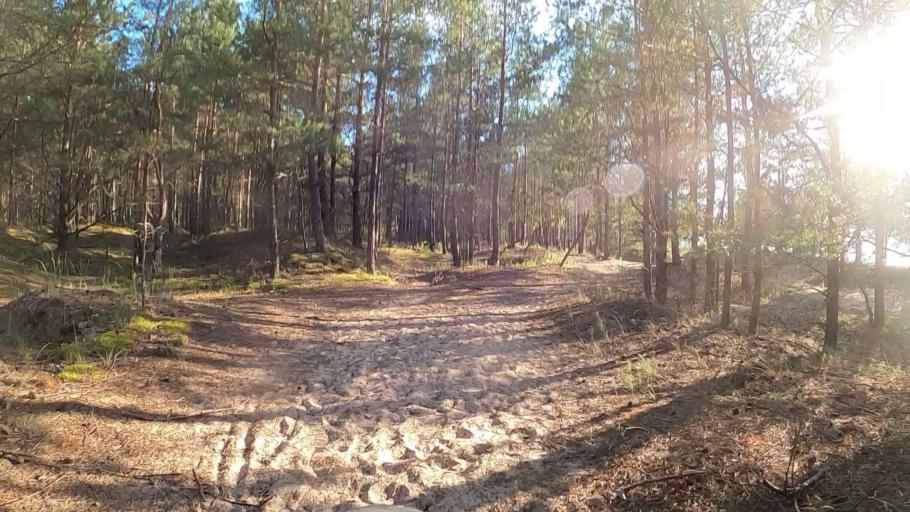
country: LV
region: Riga
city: Jaunciems
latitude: 57.1056
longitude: 24.1729
